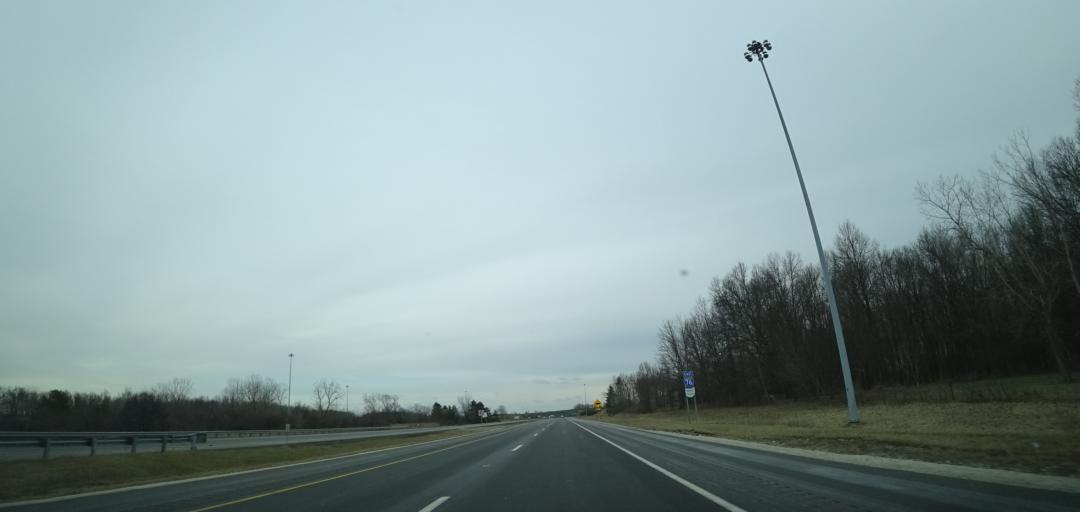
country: US
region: Ohio
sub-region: Trumbull County
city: Lordstown
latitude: 41.1088
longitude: -80.8372
